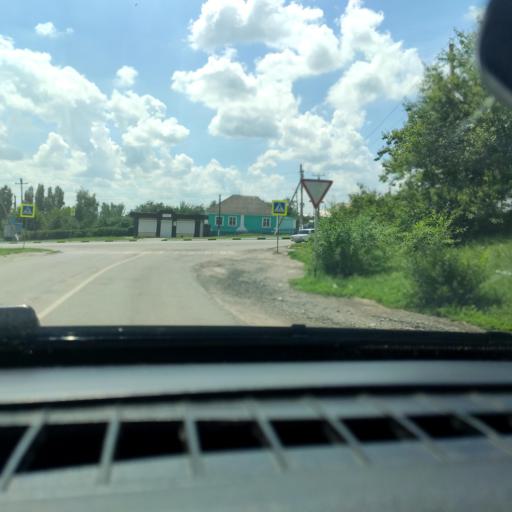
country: RU
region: Voronezj
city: Strelitsa
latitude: 51.5754
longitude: 38.7897
